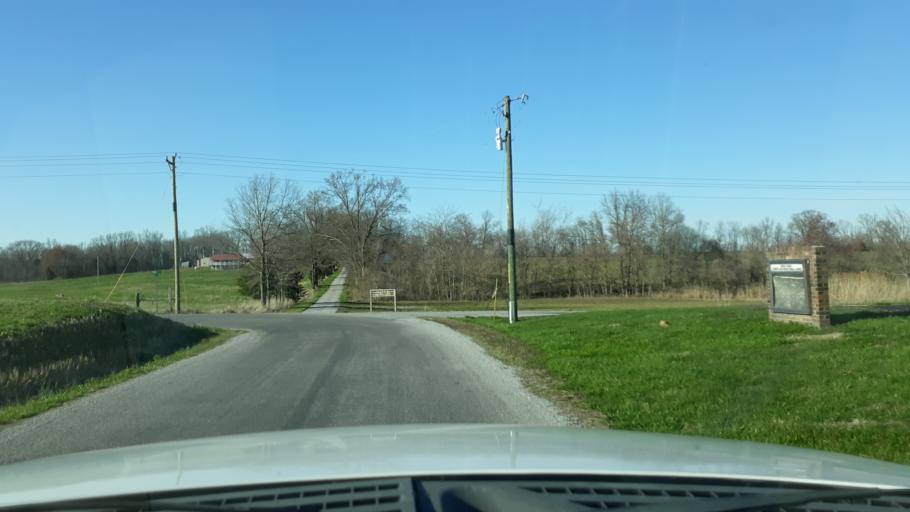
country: US
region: Illinois
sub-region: Saline County
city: Harrisburg
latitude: 37.8045
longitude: -88.6055
